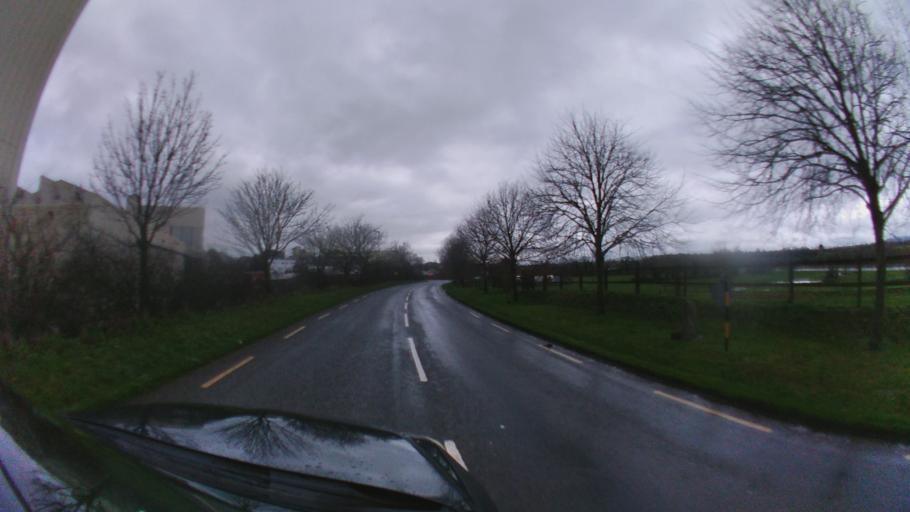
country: IE
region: Leinster
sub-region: County Carlow
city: Bagenalstown
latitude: 52.6343
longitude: -6.9944
